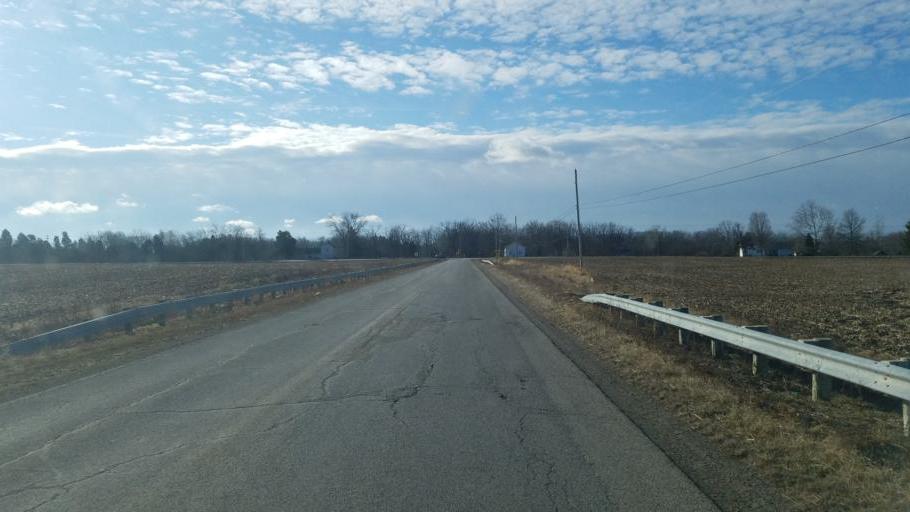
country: US
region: Ohio
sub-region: Morrow County
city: Cardington
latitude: 40.5189
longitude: -82.8641
